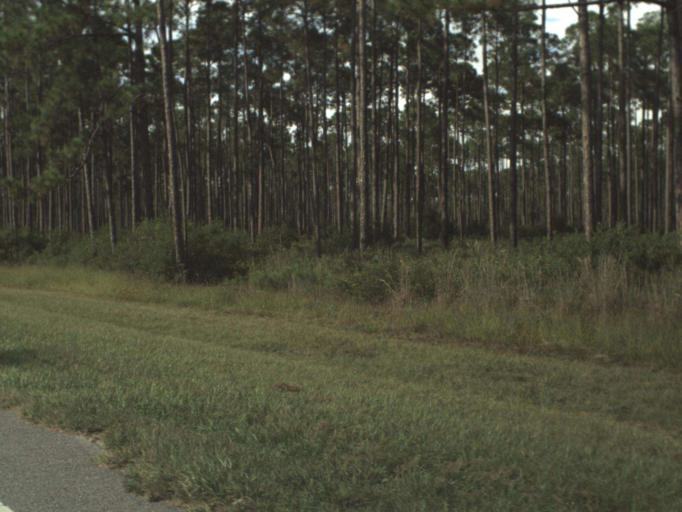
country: US
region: Florida
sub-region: Bay County
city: Mexico Beach
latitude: 30.0006
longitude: -85.5002
